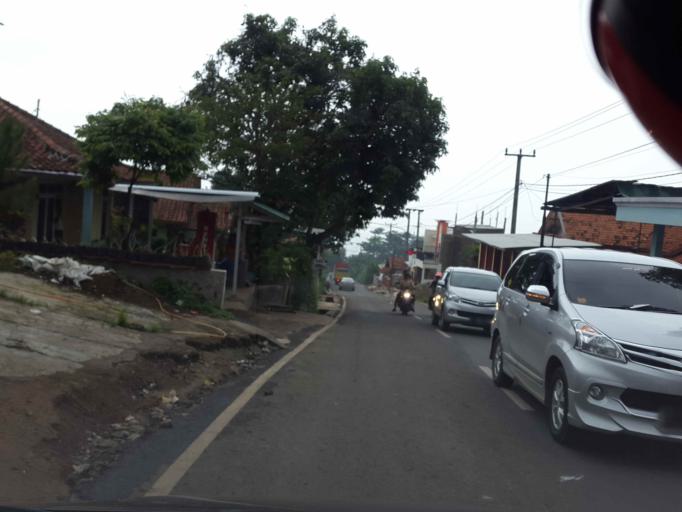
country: ID
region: West Java
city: Padalarang
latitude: -6.8324
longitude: 107.5187
